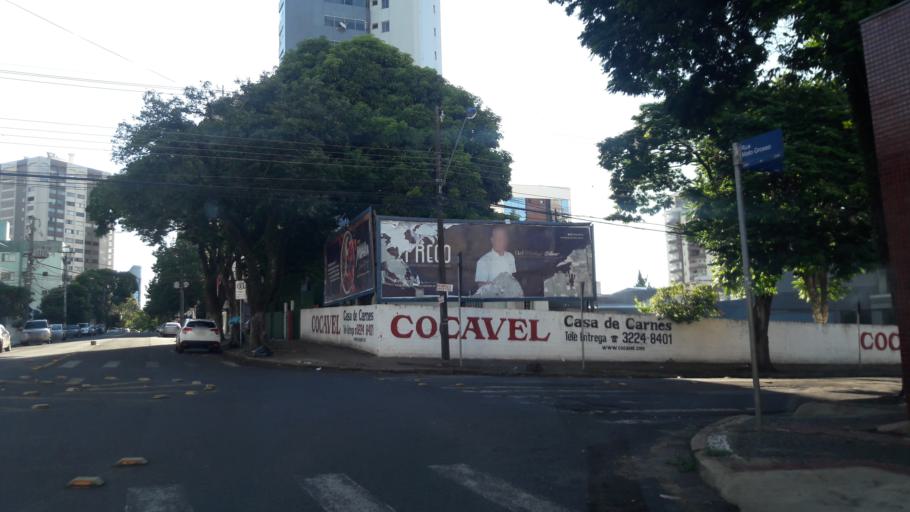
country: BR
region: Parana
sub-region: Cascavel
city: Cascavel
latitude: -24.9509
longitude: -53.4516
